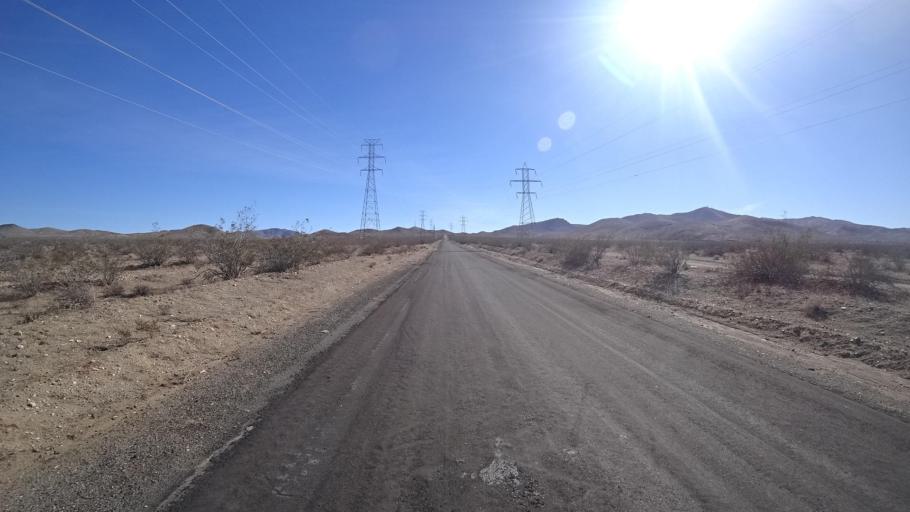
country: US
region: California
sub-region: Kern County
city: Ridgecrest
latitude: 35.3912
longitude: -117.6685
